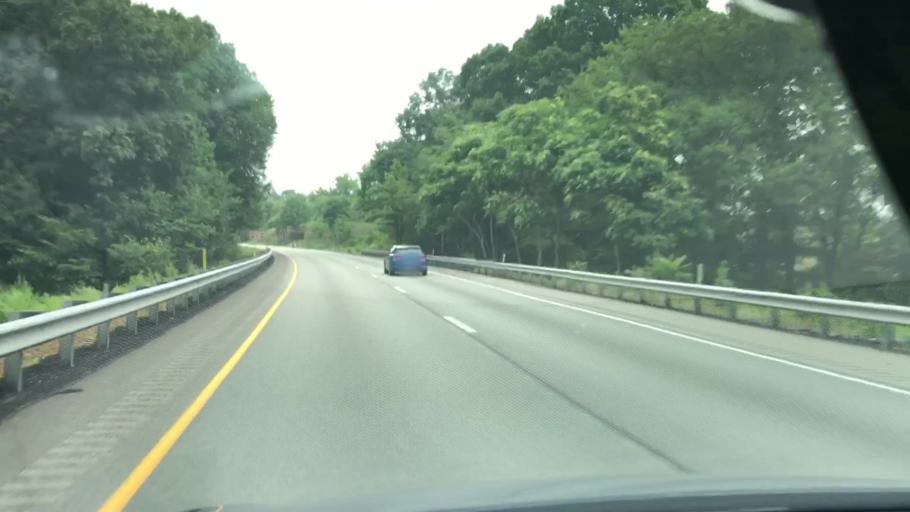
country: US
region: Pennsylvania
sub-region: Butler County
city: Zelienople
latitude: 40.7808
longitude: -80.1241
